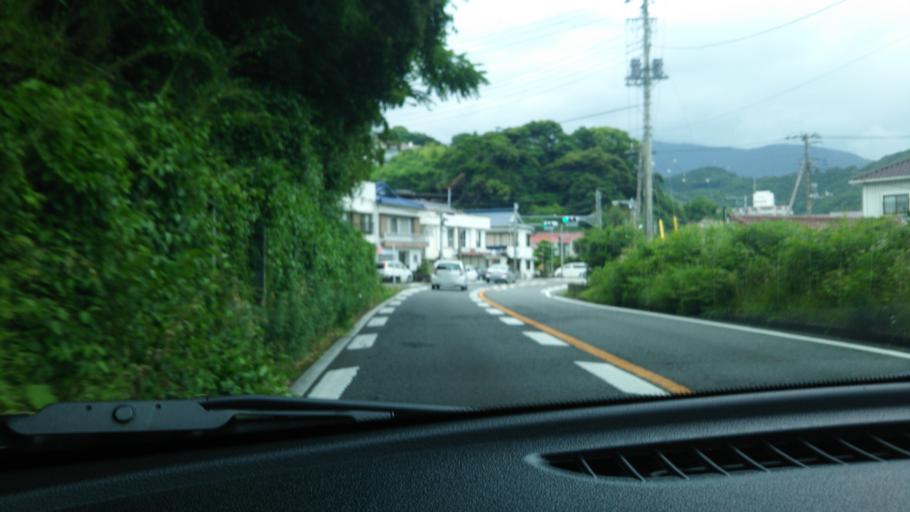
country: JP
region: Shizuoka
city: Ito
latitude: 34.8001
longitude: 139.0603
